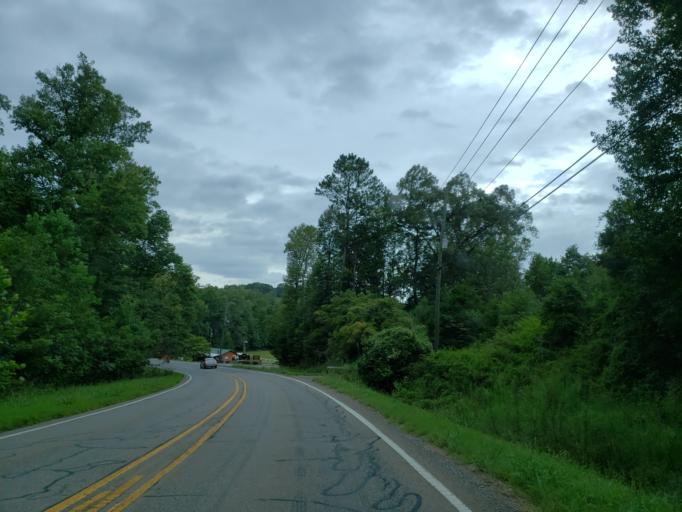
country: US
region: Georgia
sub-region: Gilmer County
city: Ellijay
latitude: 34.6402
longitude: -84.5717
